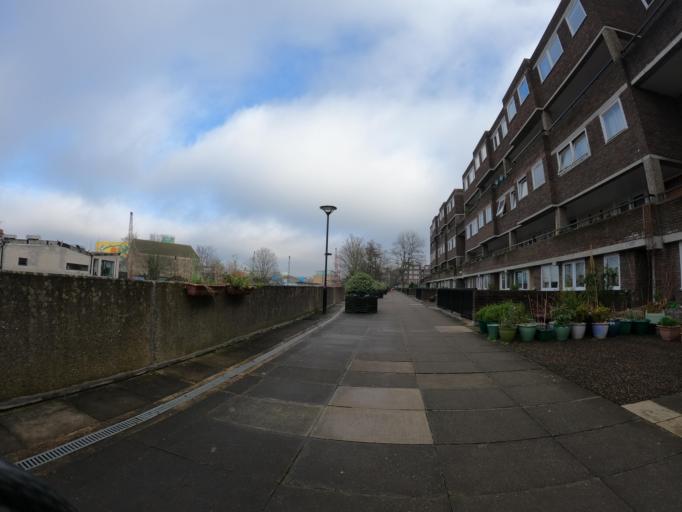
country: GB
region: England
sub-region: Greater London
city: Brentford
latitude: 51.4818
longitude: -0.3063
